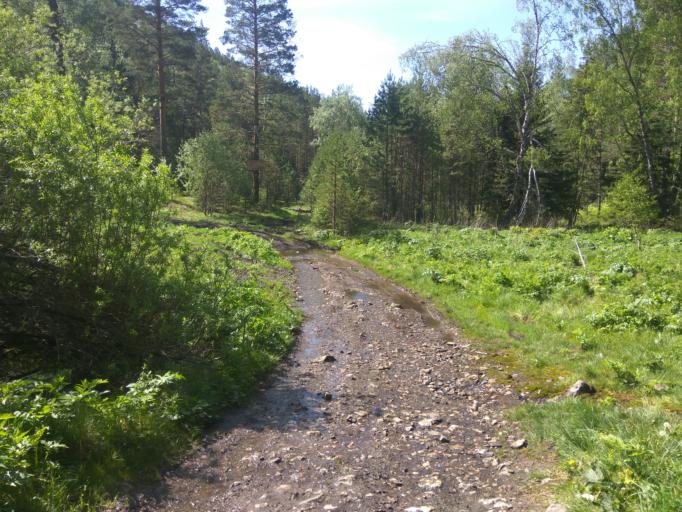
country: RU
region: Krasnoyarskiy
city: Krasnoyarsk
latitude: 55.9023
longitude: 92.9423
